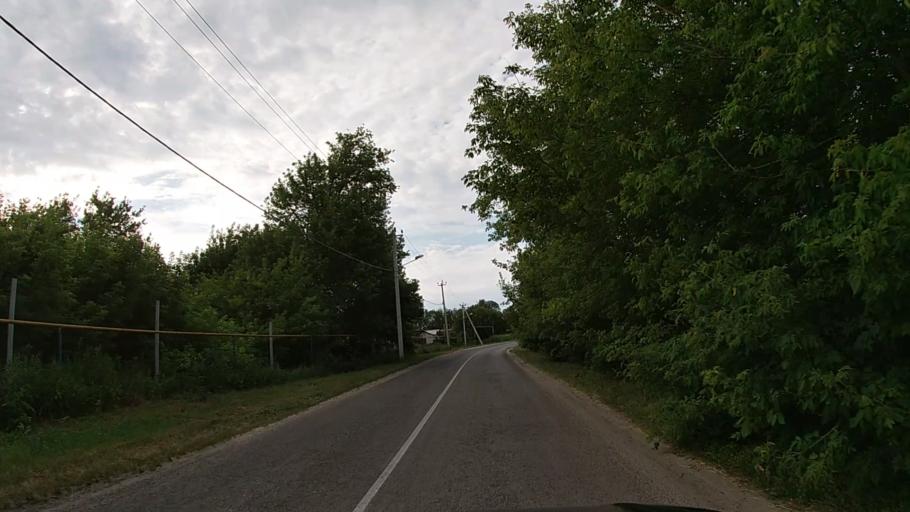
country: RU
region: Belgorod
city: Severnyy
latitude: 50.7085
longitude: 36.5999
